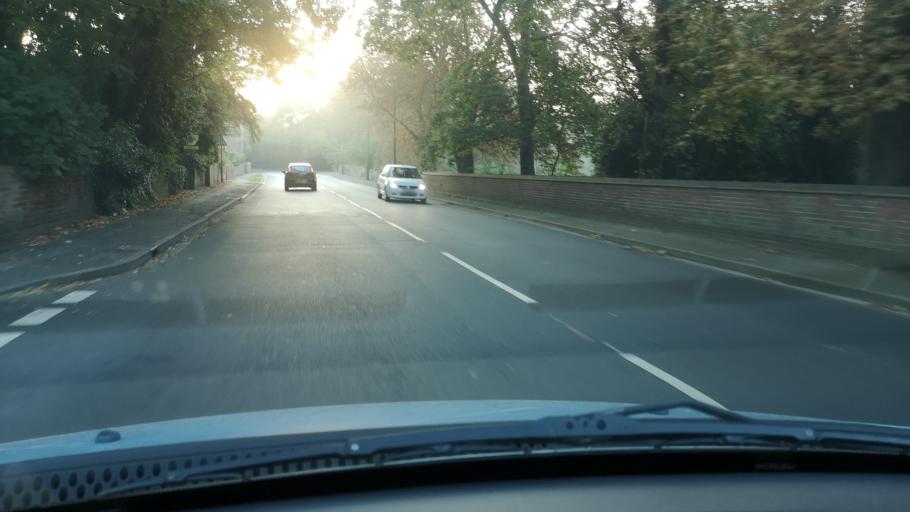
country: GB
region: England
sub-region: Doncaster
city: Hatfield
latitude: 53.5742
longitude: -1.0041
